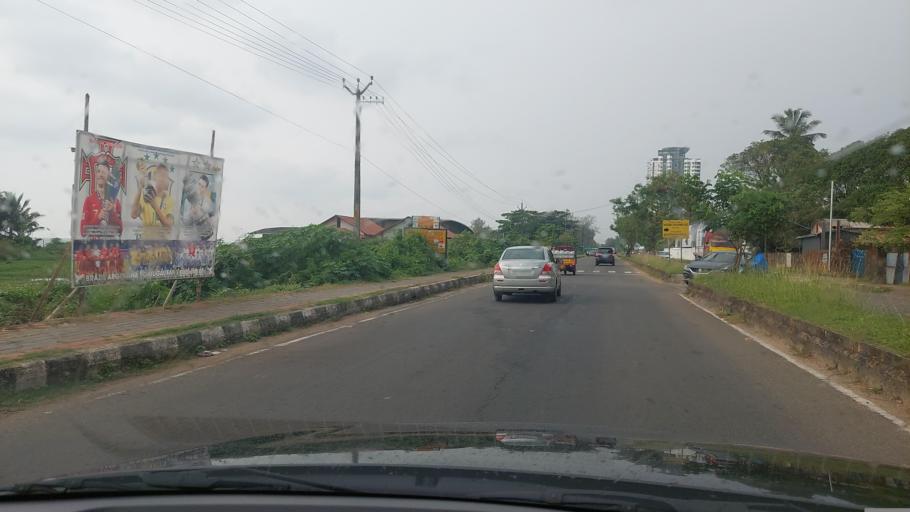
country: IN
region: Kerala
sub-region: Kozhikode
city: Kozhikode
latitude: 11.2868
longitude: 75.7600
